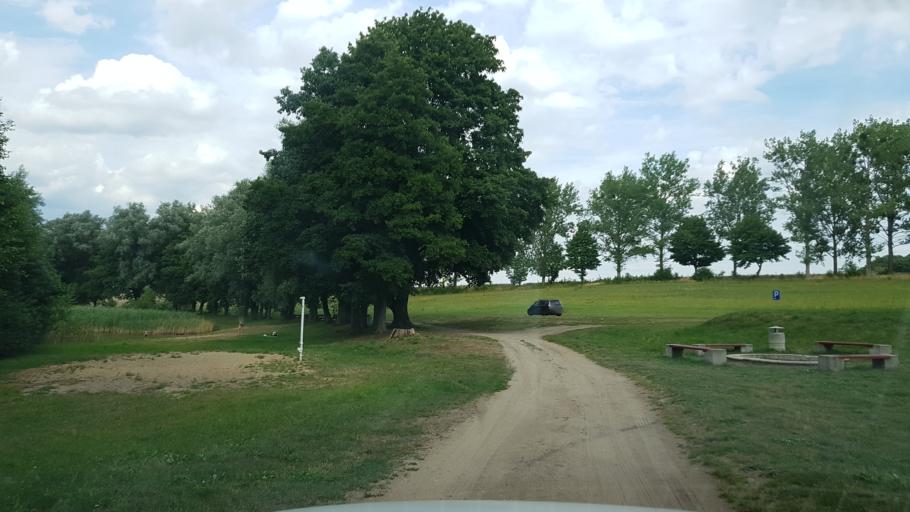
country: PL
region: West Pomeranian Voivodeship
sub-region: Powiat drawski
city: Drawsko Pomorskie
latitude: 53.5738
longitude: 15.8454
